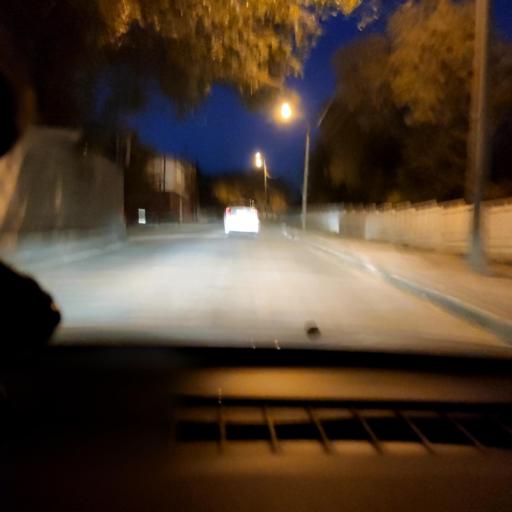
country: RU
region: Samara
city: Samara
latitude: 53.1927
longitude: 50.1568
